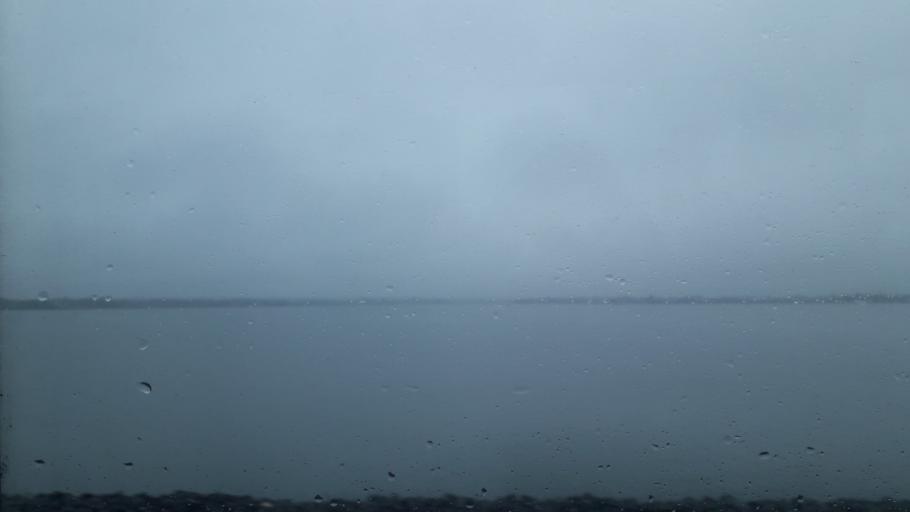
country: IE
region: Leinster
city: Malahide
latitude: 53.4628
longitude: -6.1552
